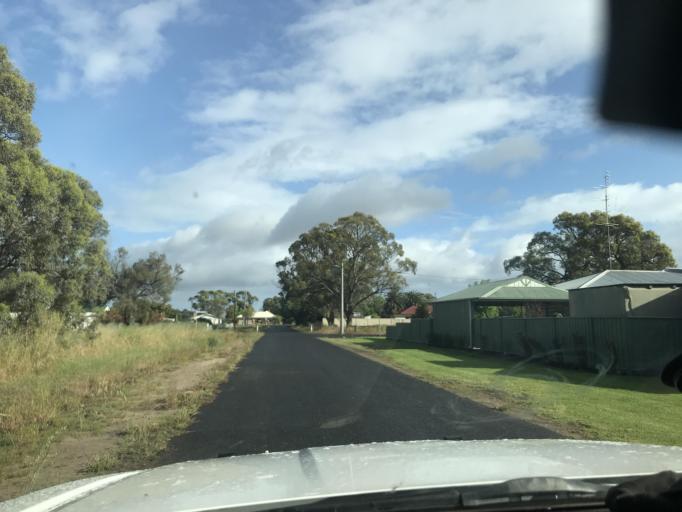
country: AU
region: Victoria
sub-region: Horsham
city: Horsham
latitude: -36.7210
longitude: 141.4708
